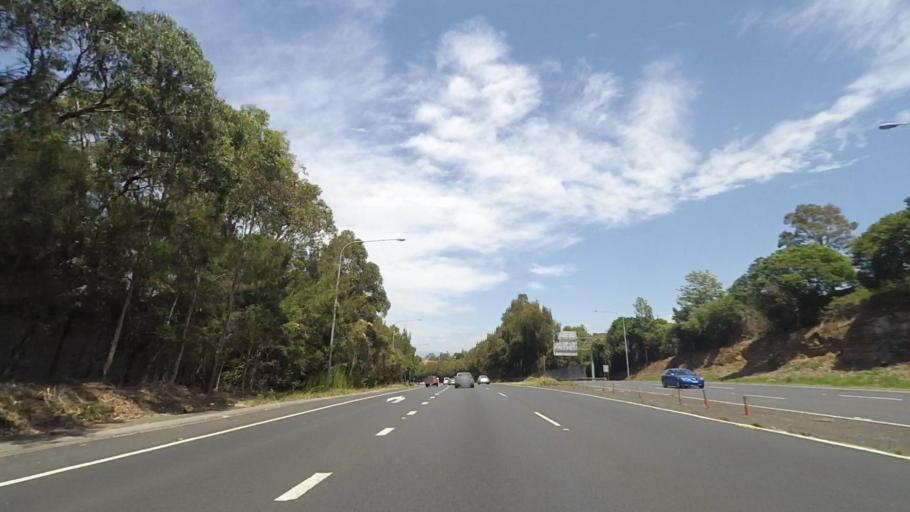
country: AU
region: New South Wales
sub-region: Wollongong
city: West Wollongong
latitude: -34.4248
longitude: 150.8684
